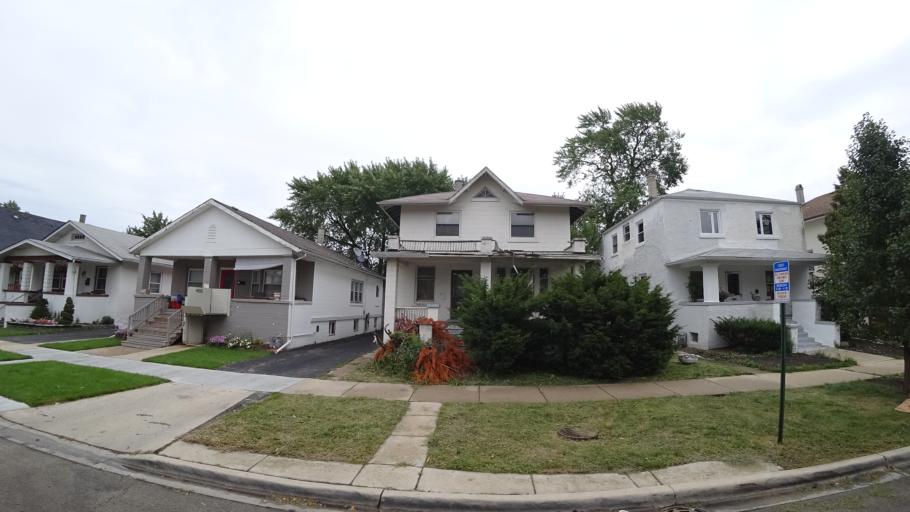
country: US
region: Illinois
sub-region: Cook County
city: Cicero
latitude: 41.8593
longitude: -87.7666
